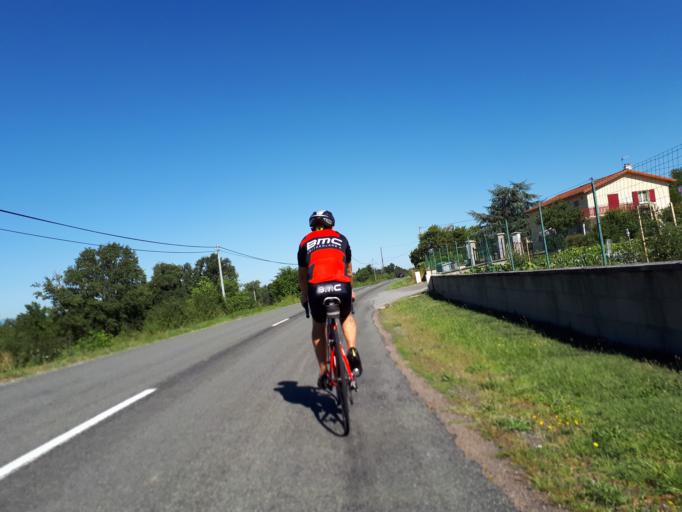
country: FR
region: Rhone-Alpes
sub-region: Departement de la Loire
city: Civens
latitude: 45.7812
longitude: 4.2478
